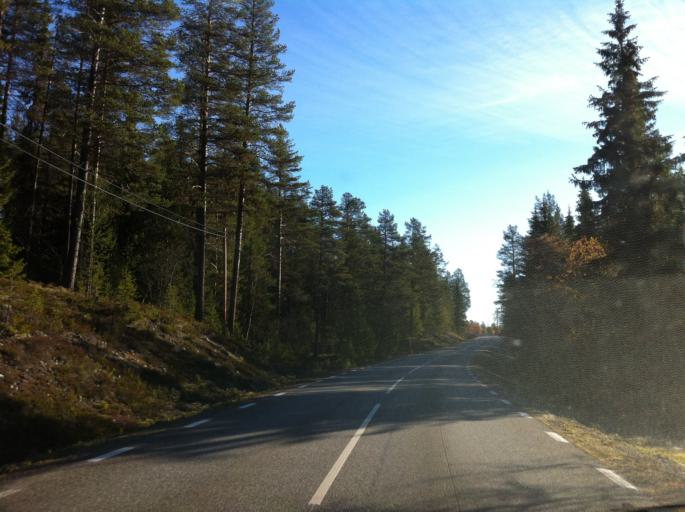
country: NO
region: Hedmark
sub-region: Engerdal
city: Engerdal
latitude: 62.0013
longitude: 12.4449
